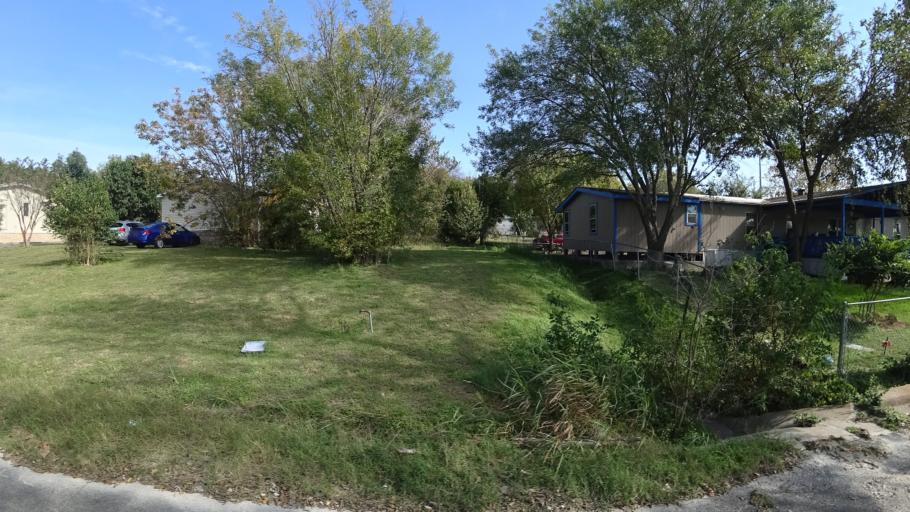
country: US
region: Texas
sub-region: Travis County
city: Pflugerville
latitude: 30.4092
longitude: -97.6322
